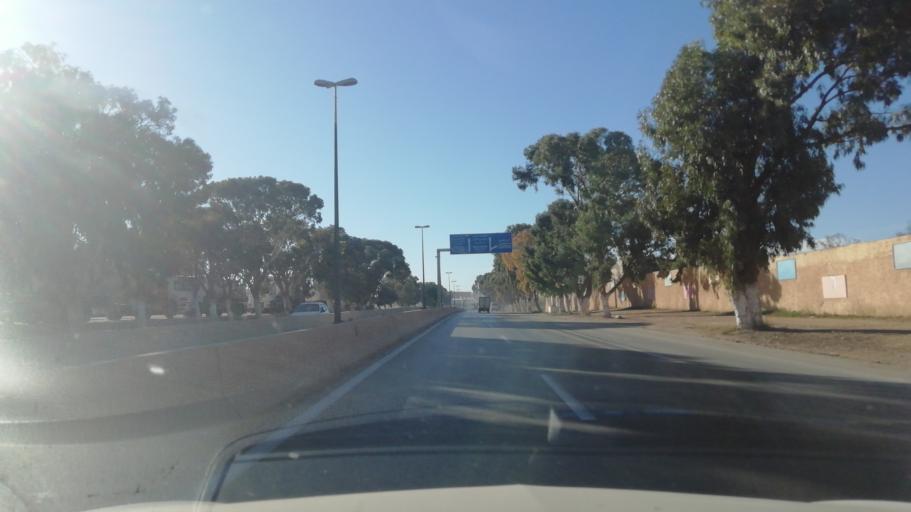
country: DZ
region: Tlemcen
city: Remchi
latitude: 35.0550
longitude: -1.4237
